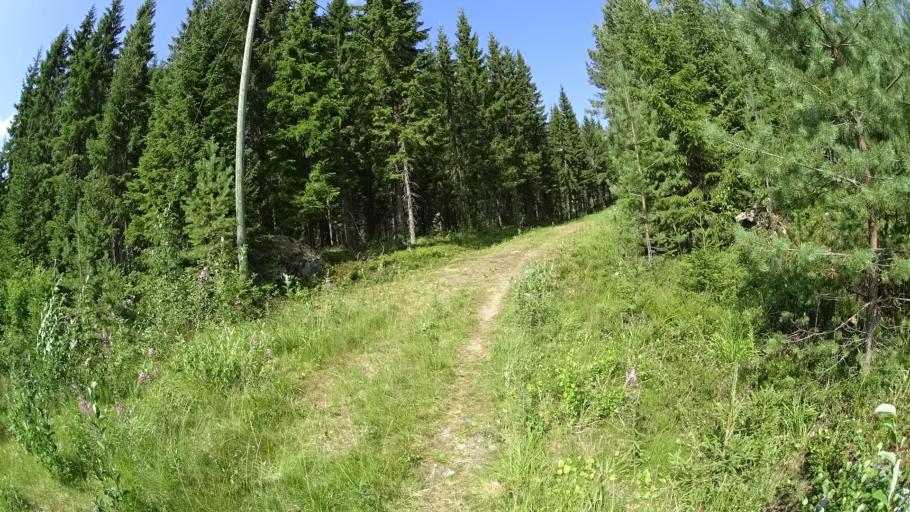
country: FI
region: North Karelia
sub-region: Pielisen Karjala
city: Lieksa
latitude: 63.1247
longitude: 29.8010
